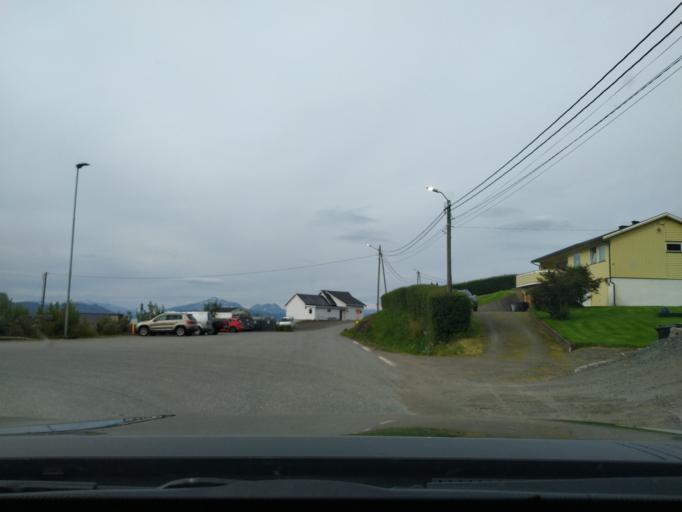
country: NO
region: Nordland
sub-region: Evenes
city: Randa
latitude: 68.7266
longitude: 16.8485
